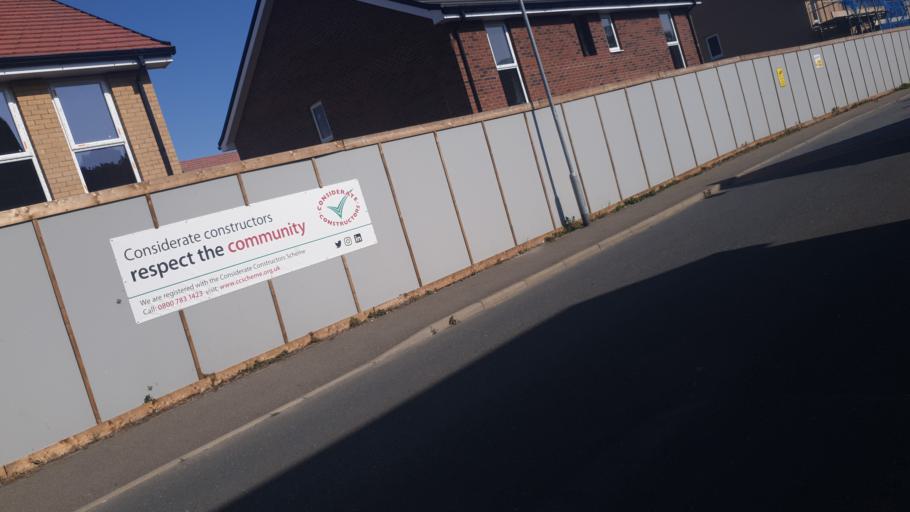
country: GB
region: England
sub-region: Essex
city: Dovercourt
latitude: 51.9391
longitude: 1.2628
